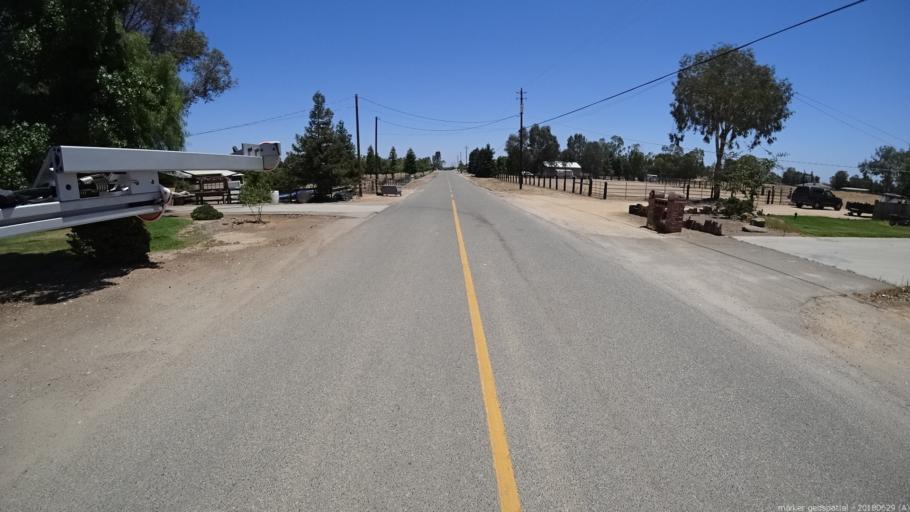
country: US
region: California
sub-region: Madera County
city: Parksdale
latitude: 36.9930
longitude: -119.9829
